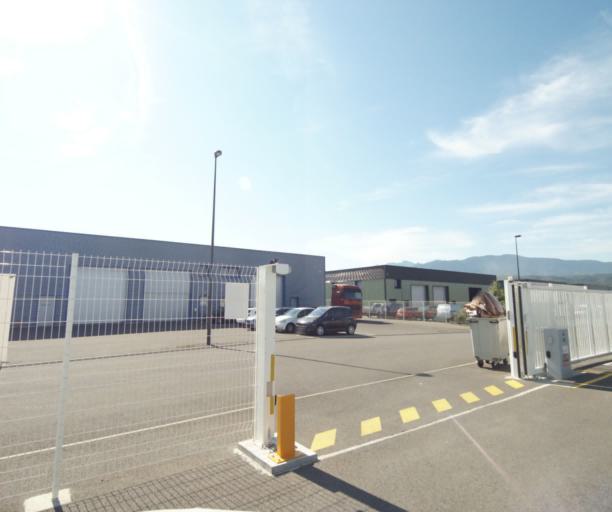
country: FR
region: Rhone-Alpes
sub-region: Departement de la Haute-Savoie
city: Marin
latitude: 46.3920
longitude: 6.5085
